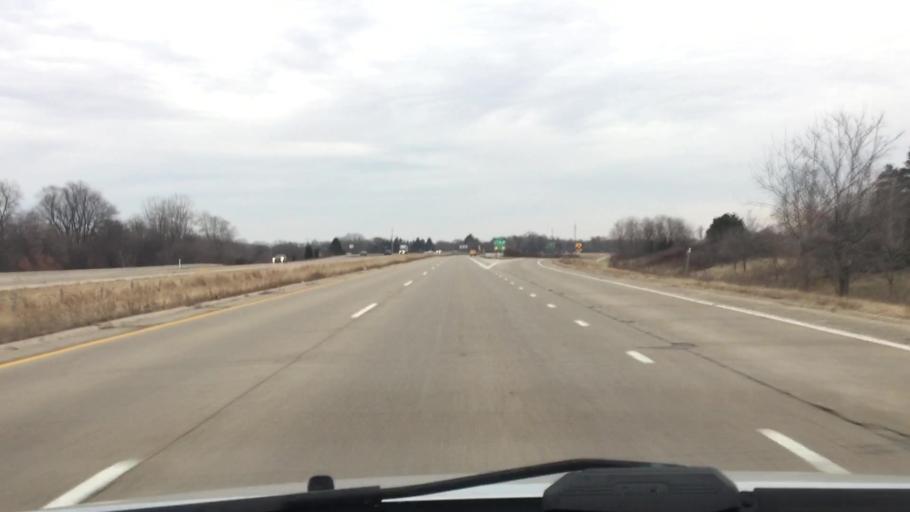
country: US
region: Wisconsin
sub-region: Waukesha County
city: Okauchee Lake
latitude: 43.1082
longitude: -88.4375
